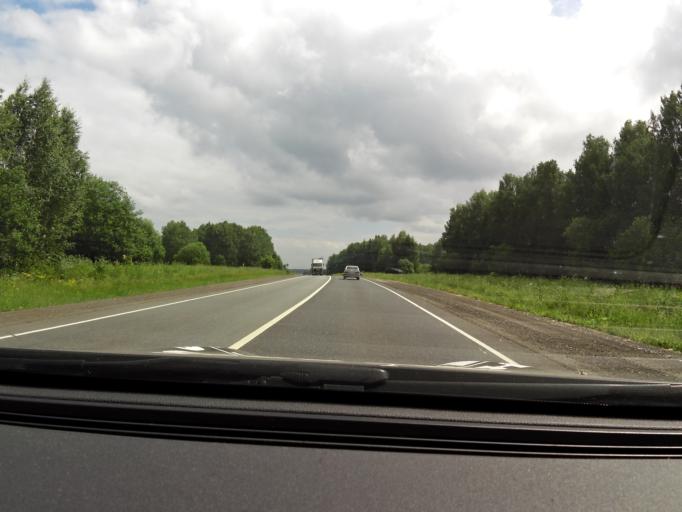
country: RU
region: Perm
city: Suksun
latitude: 57.1576
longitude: 57.2565
